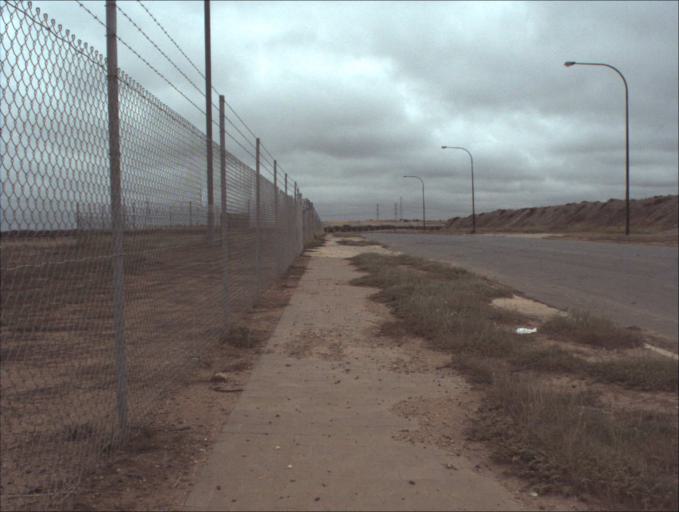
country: AU
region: South Australia
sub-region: Port Adelaide Enfield
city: Birkenhead
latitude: -34.8183
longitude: 138.5263
